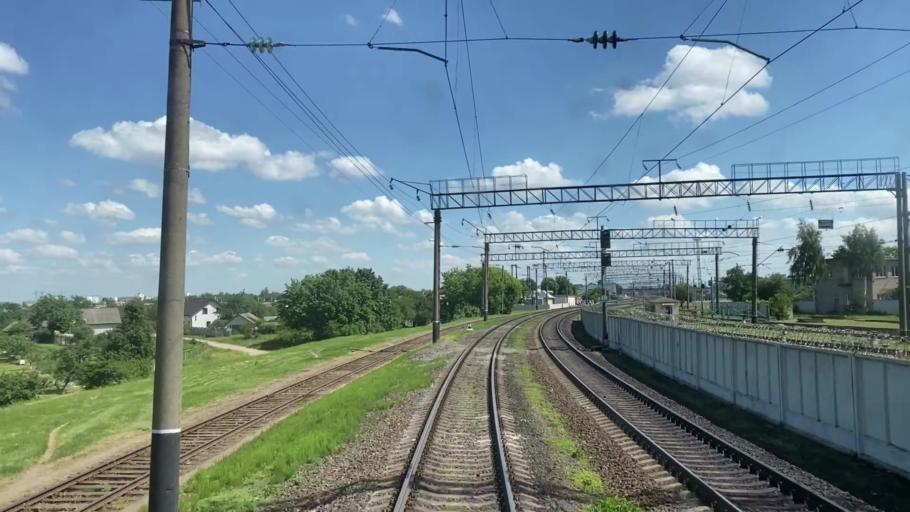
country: BY
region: Brest
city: Baranovichi
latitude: 53.1274
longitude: 25.9811
